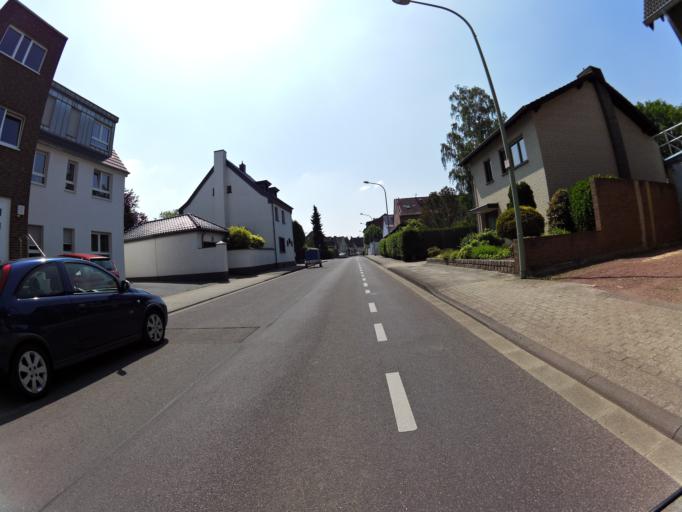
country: DE
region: North Rhine-Westphalia
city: Baesweiler
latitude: 50.9114
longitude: 6.1762
